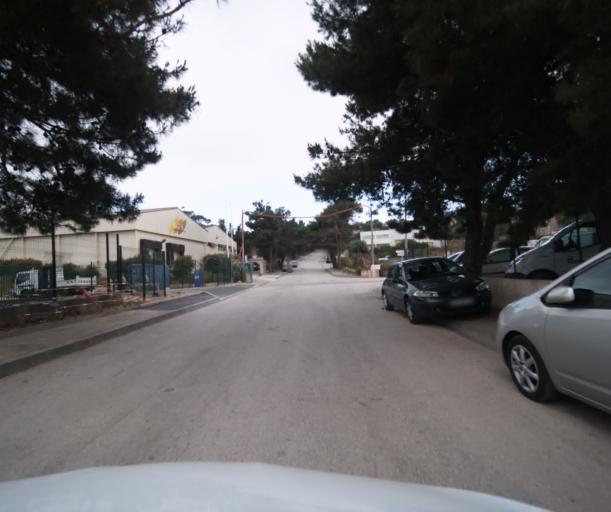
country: FR
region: Provence-Alpes-Cote d'Azur
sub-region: Departement du Var
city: La Seyne-sur-Mer
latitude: 43.1168
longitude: 5.8728
